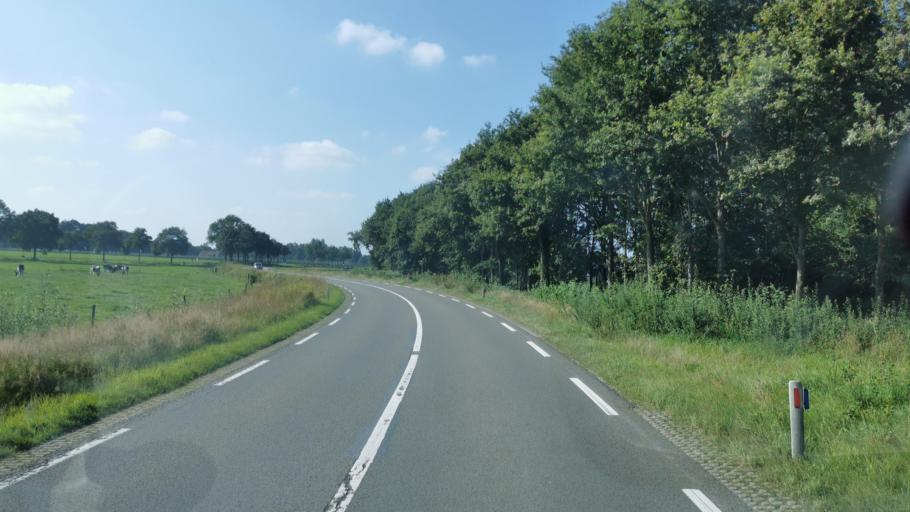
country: NL
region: Overijssel
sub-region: Gemeente Oldenzaal
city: Oldenzaal
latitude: 52.3604
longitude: 6.9219
